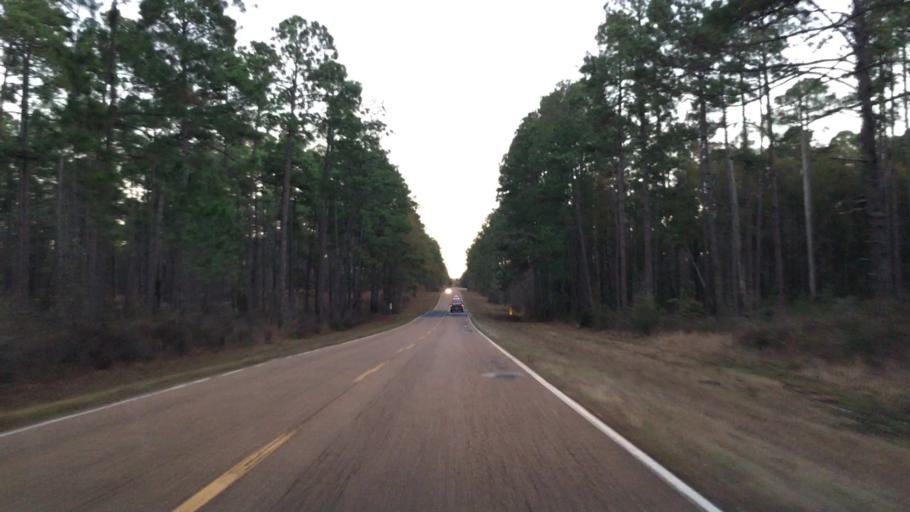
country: US
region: Louisiana
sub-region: Vernon Parish
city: Fort Polk South
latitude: 31.0105
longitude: -93.1860
